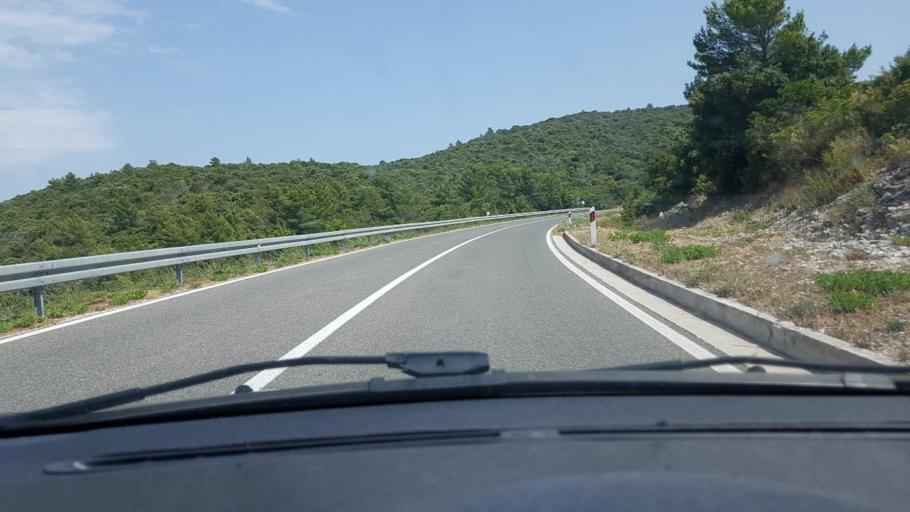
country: HR
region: Dubrovacko-Neretvanska
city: Smokvica
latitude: 42.9565
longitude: 16.9410
